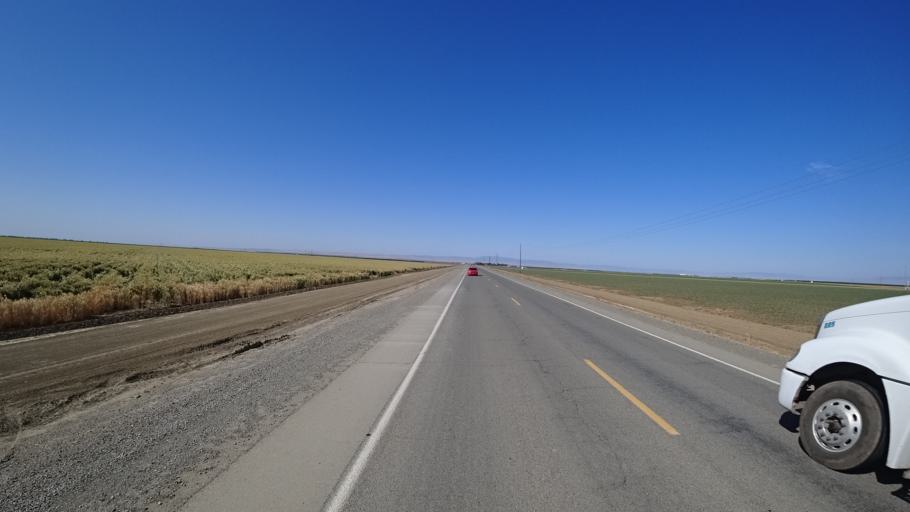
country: US
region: California
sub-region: Kings County
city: Lemoore Station
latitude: 36.1952
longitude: -119.9379
